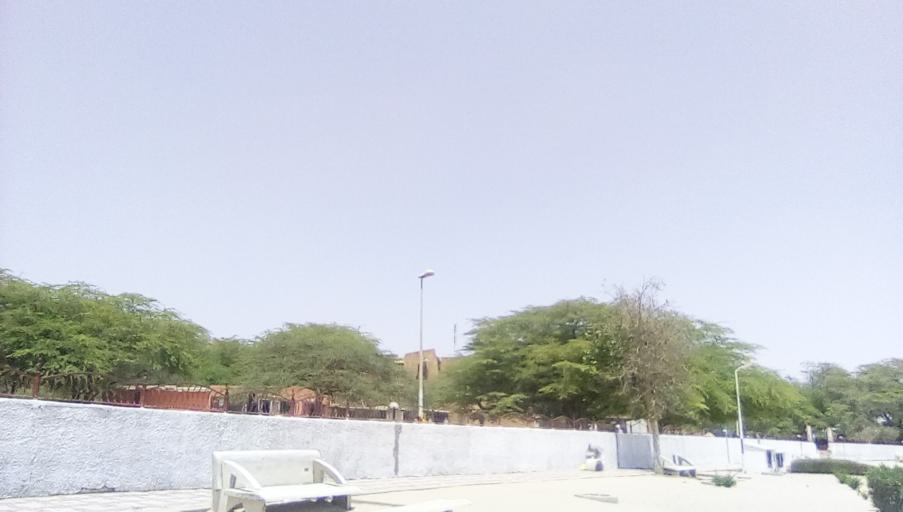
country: SN
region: Saint-Louis
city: Saint-Louis
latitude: 16.0659
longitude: -16.4230
